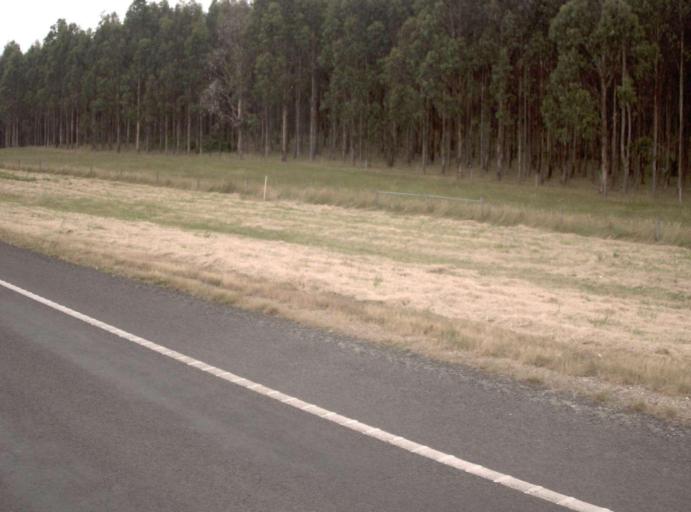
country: AU
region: Victoria
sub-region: Latrobe
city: Morwell
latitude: -38.2420
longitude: 146.3378
